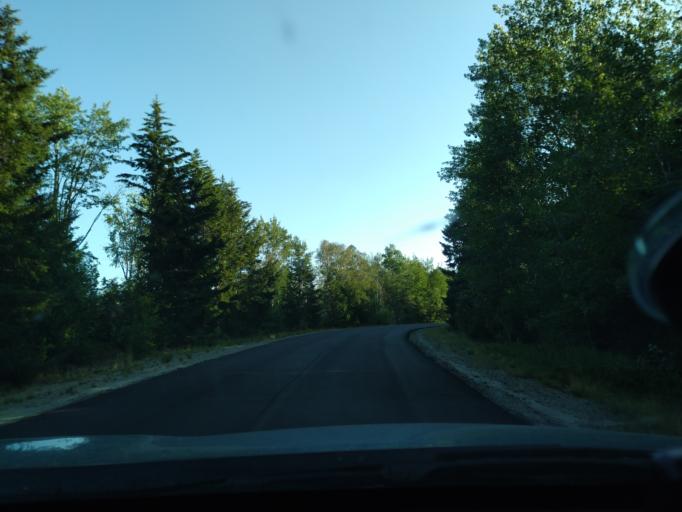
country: US
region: Maine
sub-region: Washington County
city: East Machias
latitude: 44.7092
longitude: -67.1445
